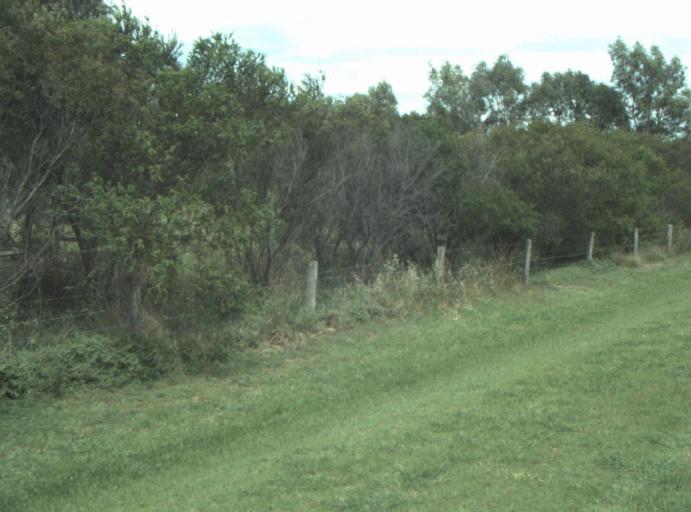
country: AU
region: Victoria
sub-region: Greater Geelong
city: Clifton Springs
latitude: -38.1351
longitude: 144.6254
